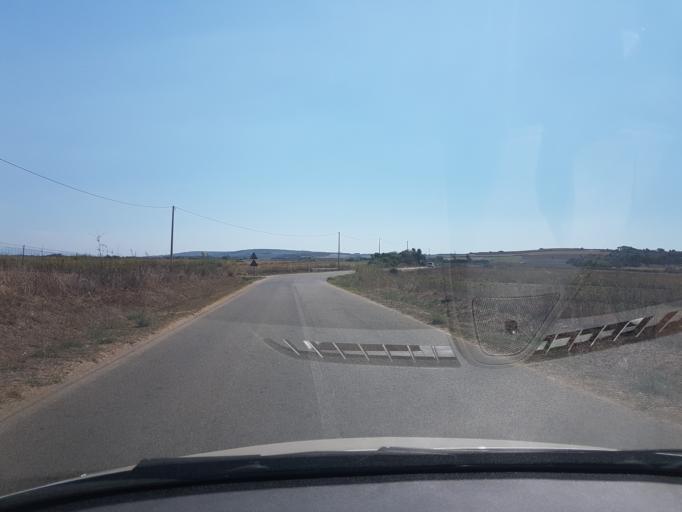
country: IT
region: Sardinia
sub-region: Provincia di Oristano
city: Nurachi
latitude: 39.9879
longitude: 8.4591
